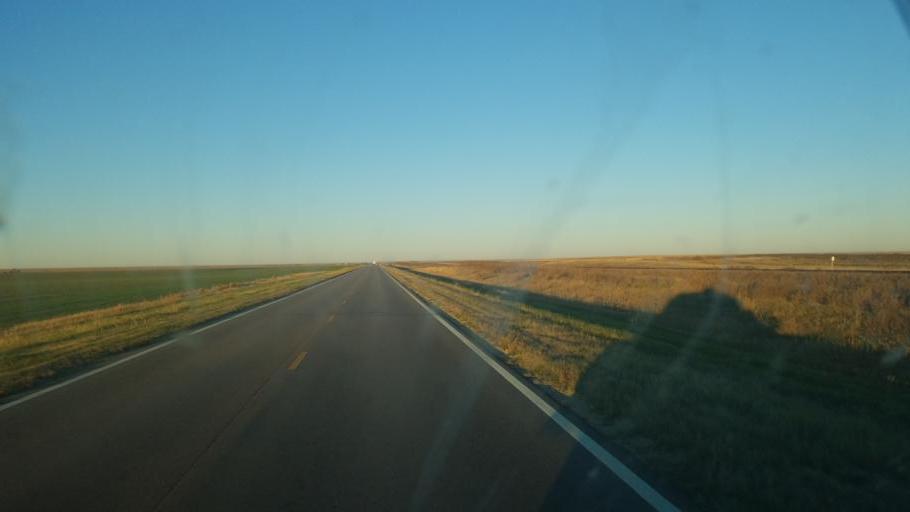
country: US
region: Kansas
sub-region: Wallace County
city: Sharon Springs
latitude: 38.8639
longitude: -102.0010
